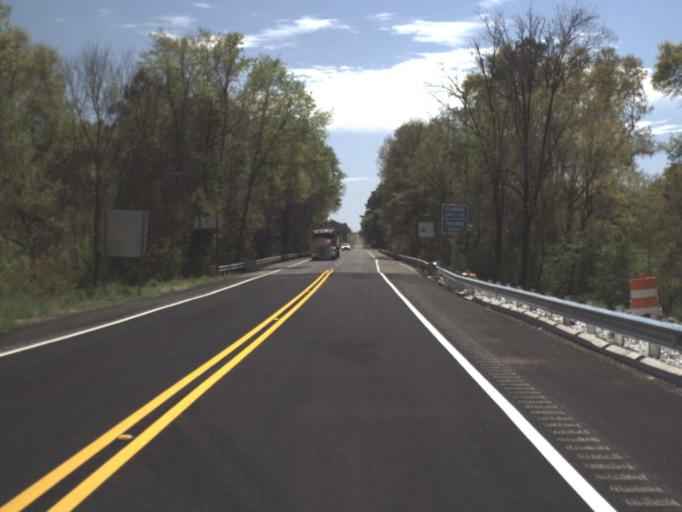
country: US
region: Alabama
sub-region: Geneva County
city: Samson
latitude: 30.9933
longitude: -85.9973
